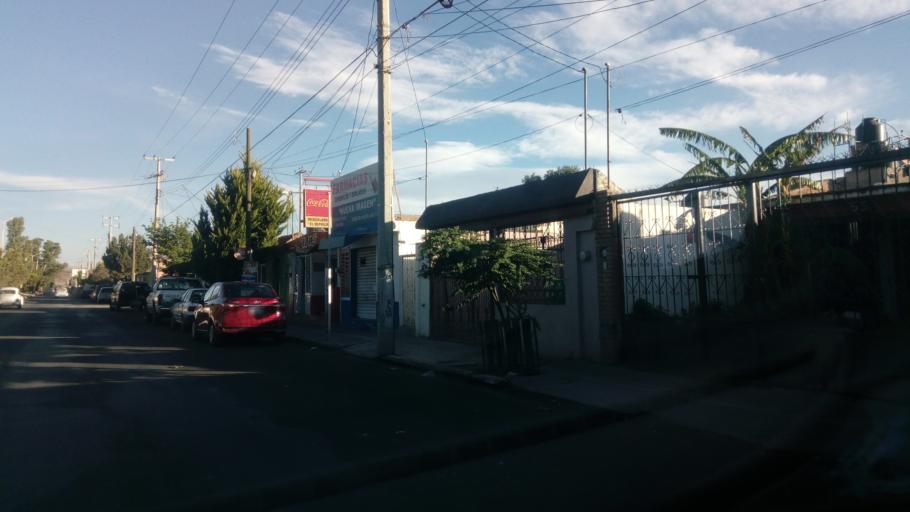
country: MX
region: Durango
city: Victoria de Durango
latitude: 24.0624
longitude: -104.5958
